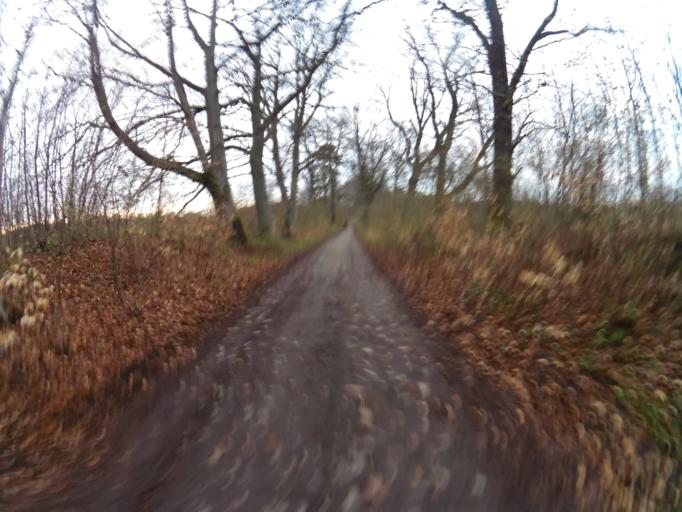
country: PL
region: West Pomeranian Voivodeship
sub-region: Powiat szczecinecki
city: Borne Sulinowo
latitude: 53.6536
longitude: 16.5107
